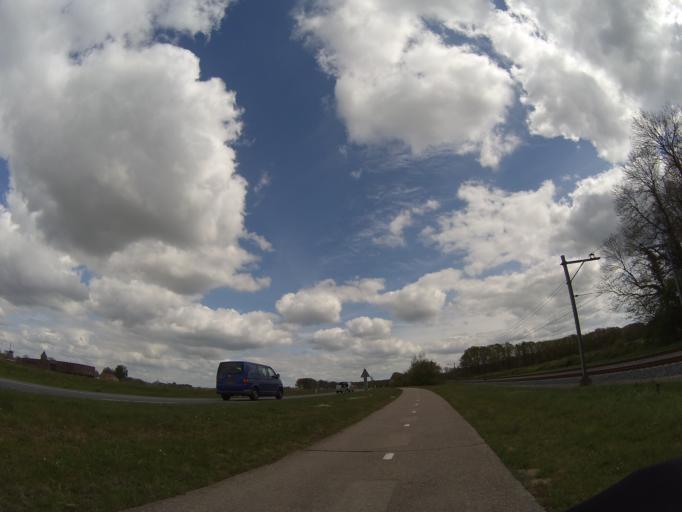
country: NL
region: Overijssel
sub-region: Gemeente Dalfsen
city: Dalfsen
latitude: 52.5001
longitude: 6.2523
